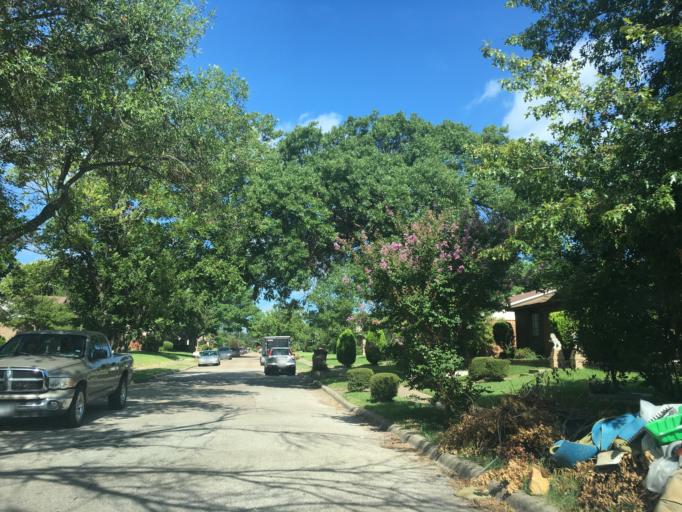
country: US
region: Texas
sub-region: Dallas County
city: Garland
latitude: 32.8507
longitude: -96.6599
